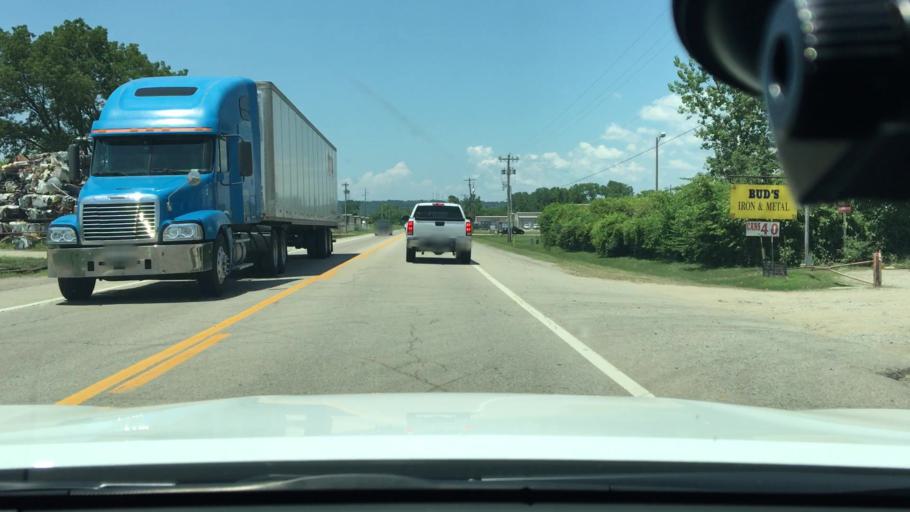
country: US
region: Arkansas
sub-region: Crawford County
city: Van Buren
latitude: 35.4151
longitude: -94.3315
